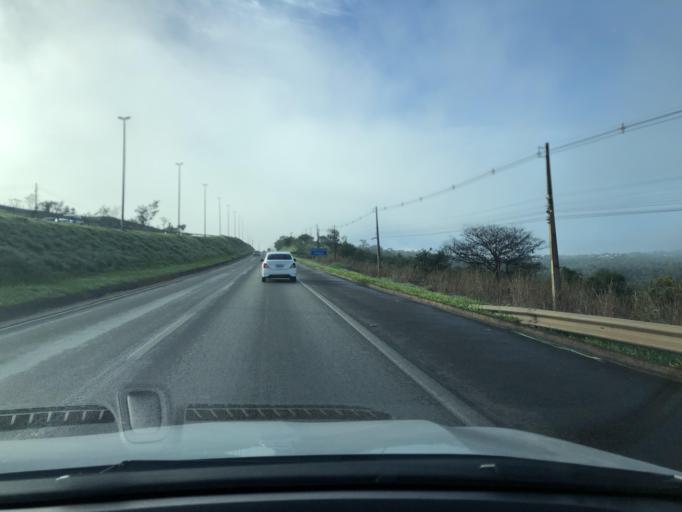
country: BR
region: Goias
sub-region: Luziania
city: Luziania
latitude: -16.1893
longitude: -47.9276
